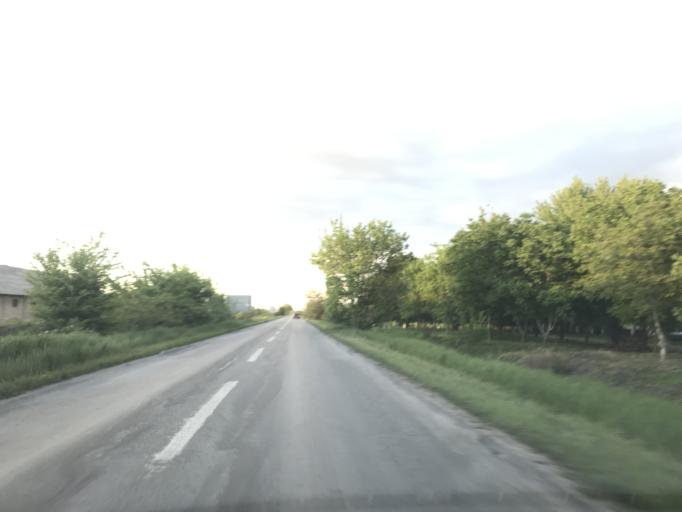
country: RS
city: Banatsko Karadordevo
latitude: 45.5913
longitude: 20.5567
